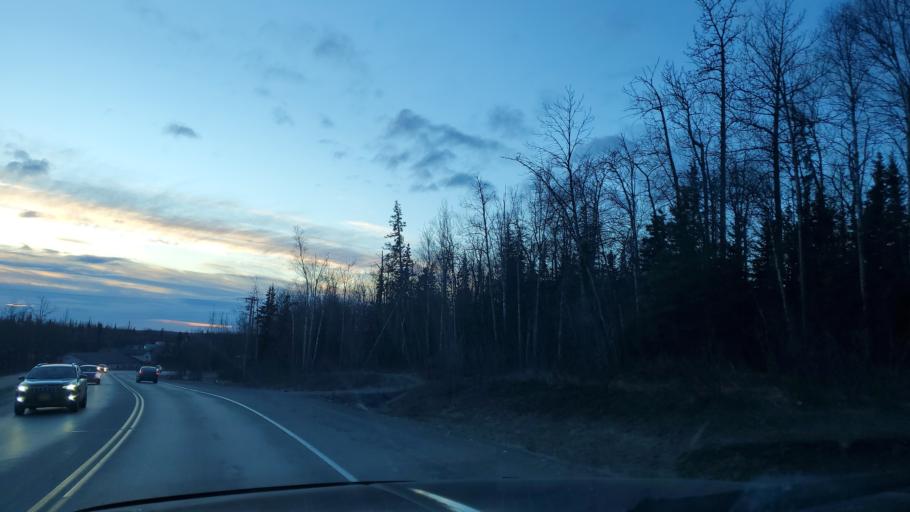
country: US
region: Alaska
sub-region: Matanuska-Susitna Borough
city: Wasilla
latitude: 61.5963
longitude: -149.4299
